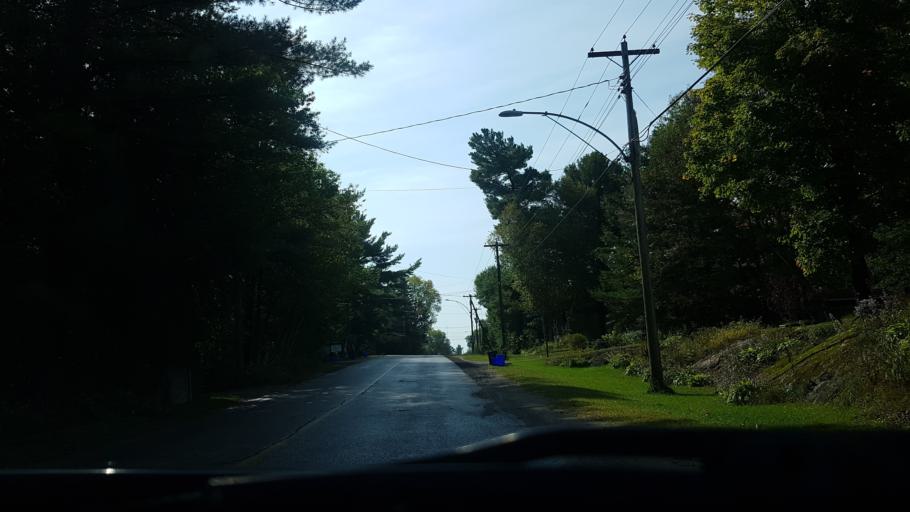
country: CA
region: Ontario
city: Gravenhurst
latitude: 44.7560
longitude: -79.3328
